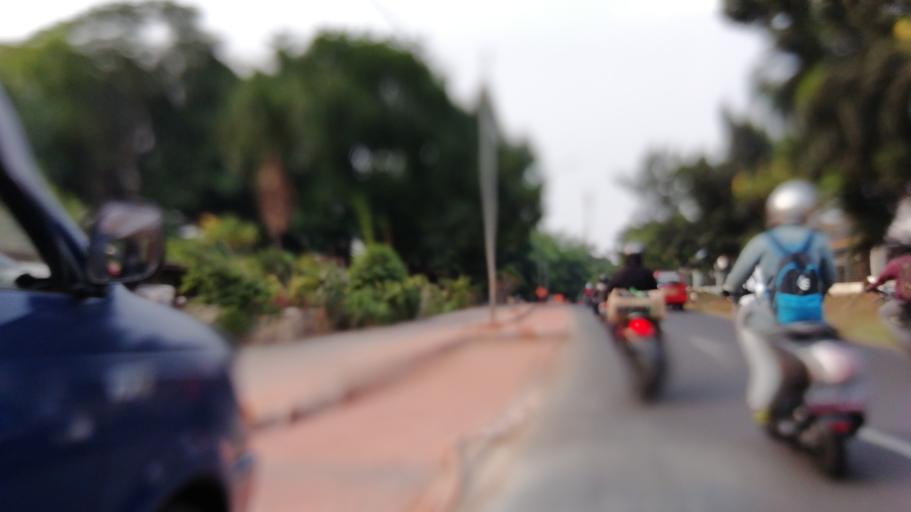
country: ID
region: West Java
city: Depok
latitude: -6.3494
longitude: 106.8326
